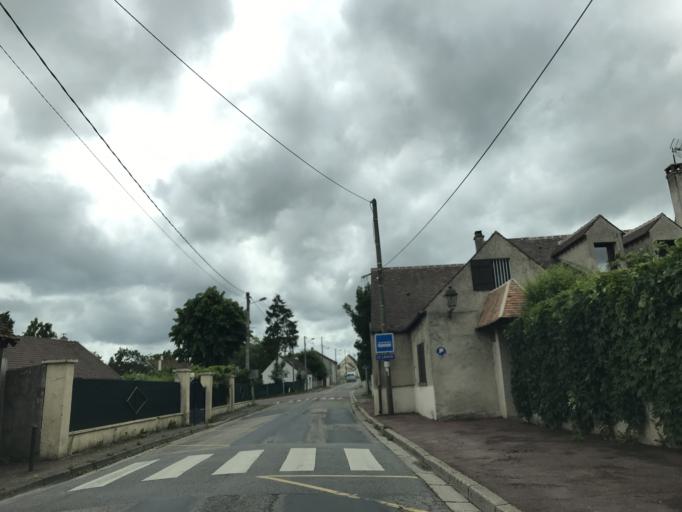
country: FR
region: Ile-de-France
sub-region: Departement des Yvelines
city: Rosny-sur-Seine
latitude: 48.9764
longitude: 1.5887
